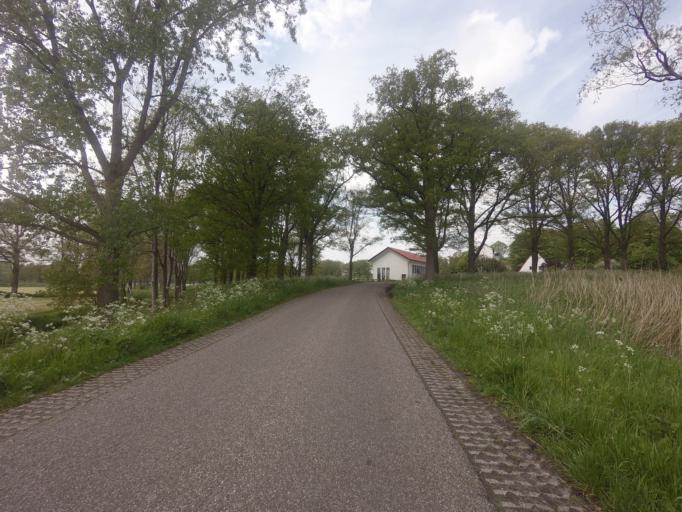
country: NL
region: Overijssel
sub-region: Gemeente Hof van Twente
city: Delden
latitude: 52.2453
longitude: 6.6785
